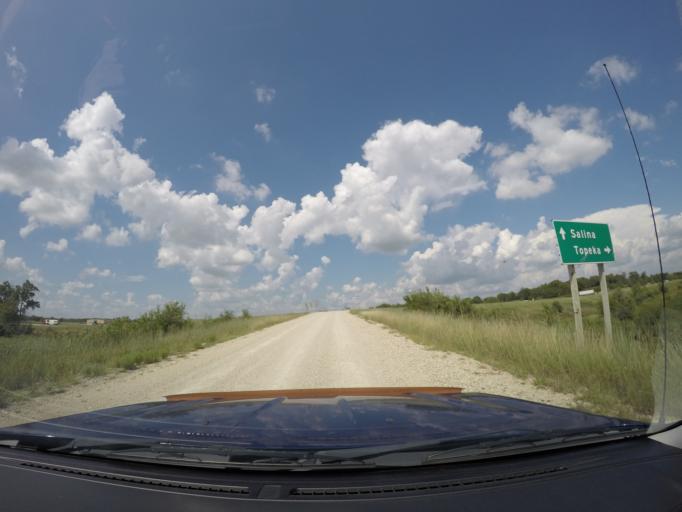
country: US
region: Kansas
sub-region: Wabaunsee County
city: Alma
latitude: 39.0639
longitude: -96.3539
